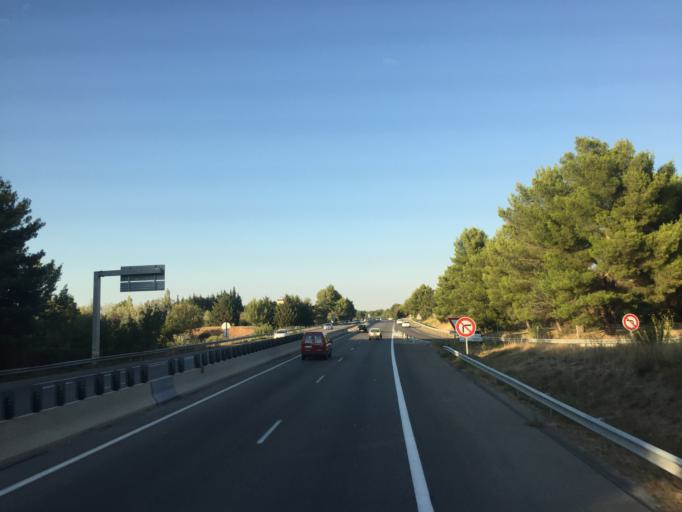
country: FR
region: Provence-Alpes-Cote d'Azur
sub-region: Departement des Bouches-du-Rhone
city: Venelles
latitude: 43.5732
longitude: 5.4690
